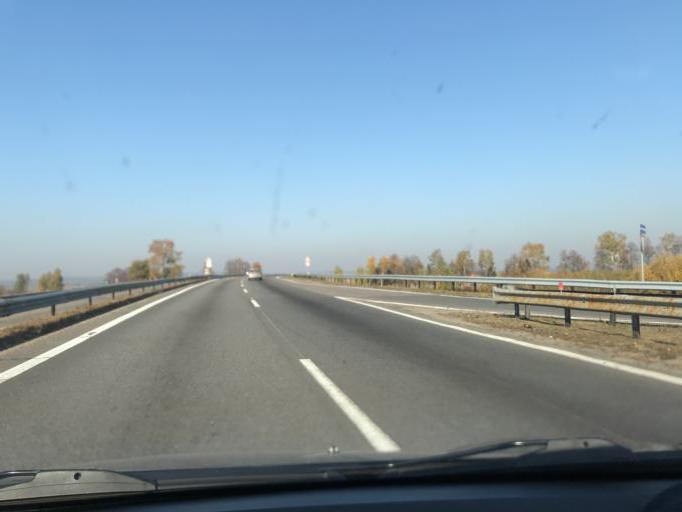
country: BY
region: Minsk
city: Luhavaya Slabada
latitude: 53.7893
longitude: 27.8200
